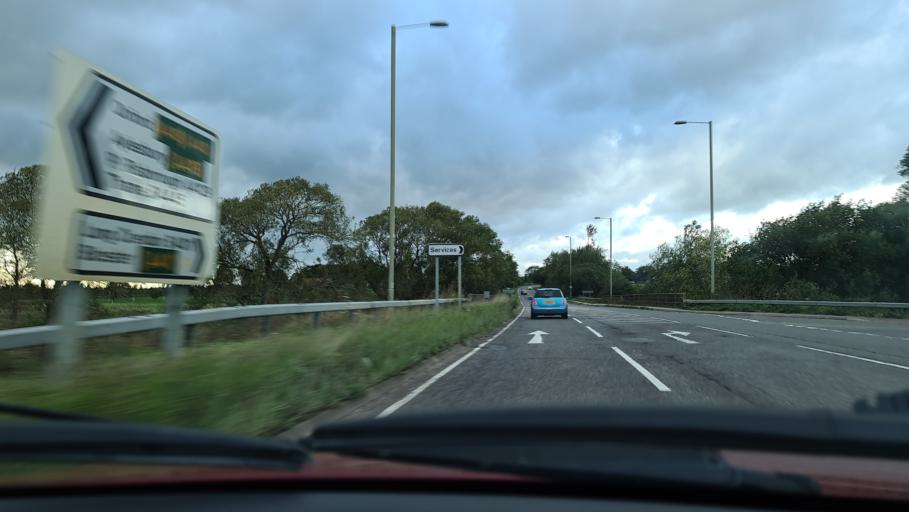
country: GB
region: England
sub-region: Oxfordshire
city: Thame
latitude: 51.7566
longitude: -0.9799
